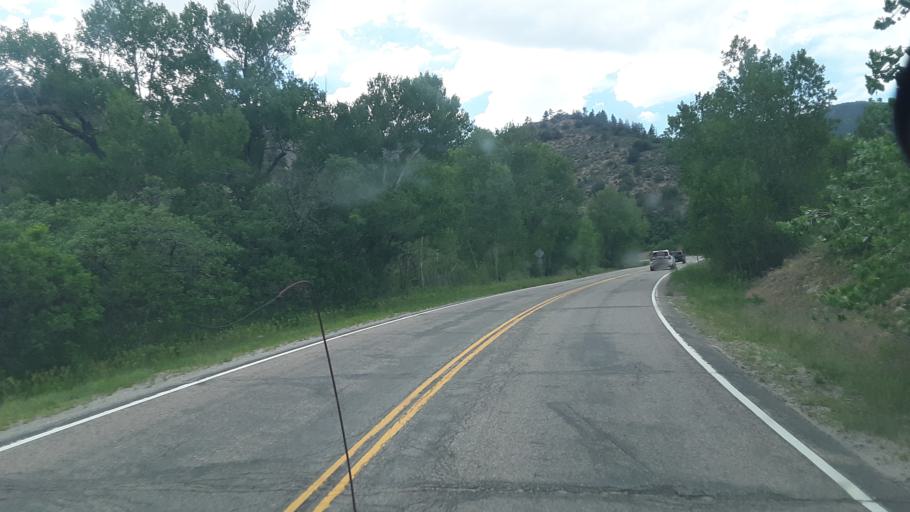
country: US
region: Colorado
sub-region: Fremont County
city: Florence
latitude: 38.1735
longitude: -105.1458
